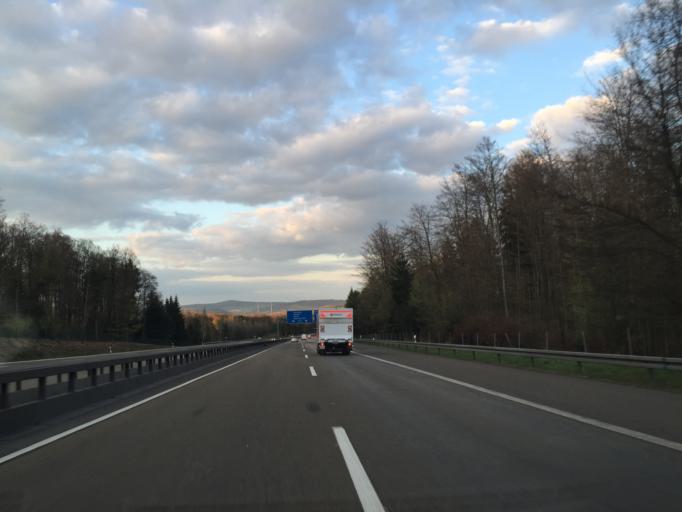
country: DE
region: Hesse
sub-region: Regierungsbezirk Kassel
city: Oberaula
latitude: 50.8046
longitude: 9.5031
